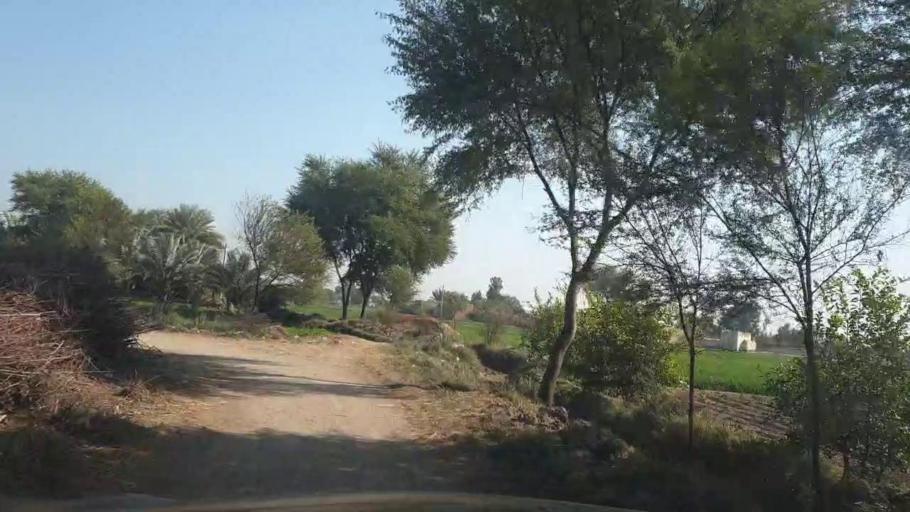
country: PK
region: Sindh
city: Mirpur Mathelo
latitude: 27.9824
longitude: 69.4725
